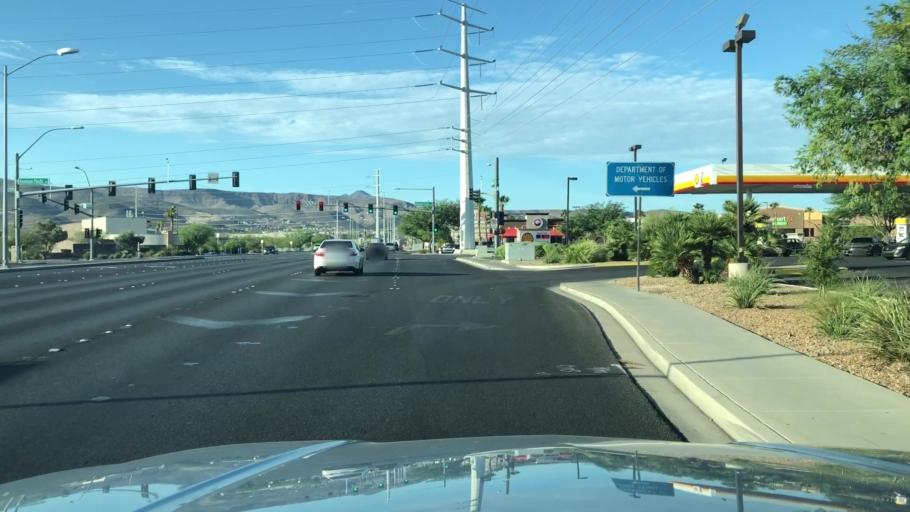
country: US
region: Nevada
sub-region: Clark County
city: Whitney
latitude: 36.0426
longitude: -115.0469
